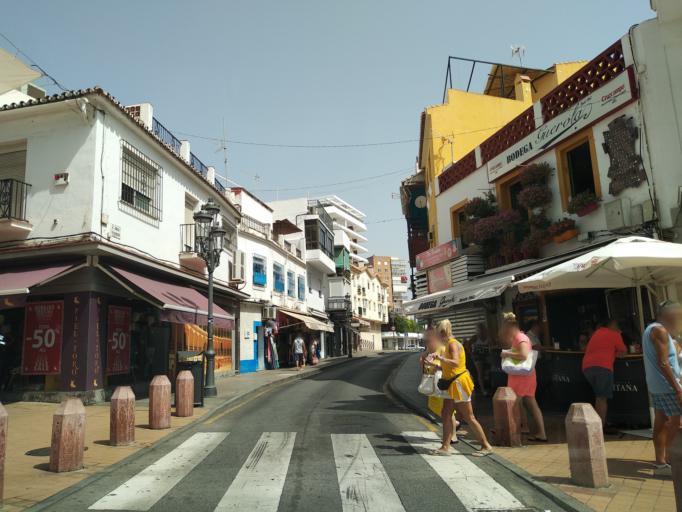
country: ES
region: Andalusia
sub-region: Provincia de Malaga
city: Torremolinos
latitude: 36.6225
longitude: -4.4978
